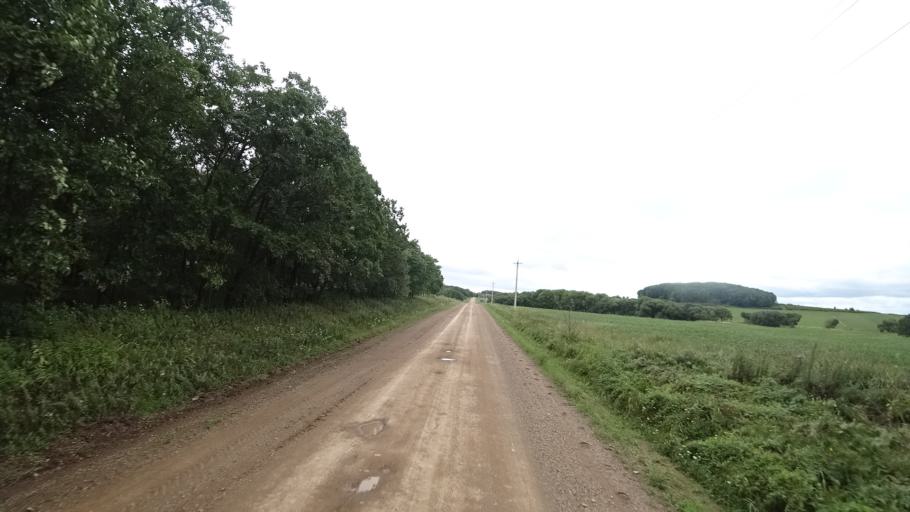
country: RU
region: Primorskiy
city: Chernigovka
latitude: 44.4680
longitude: 132.5852
